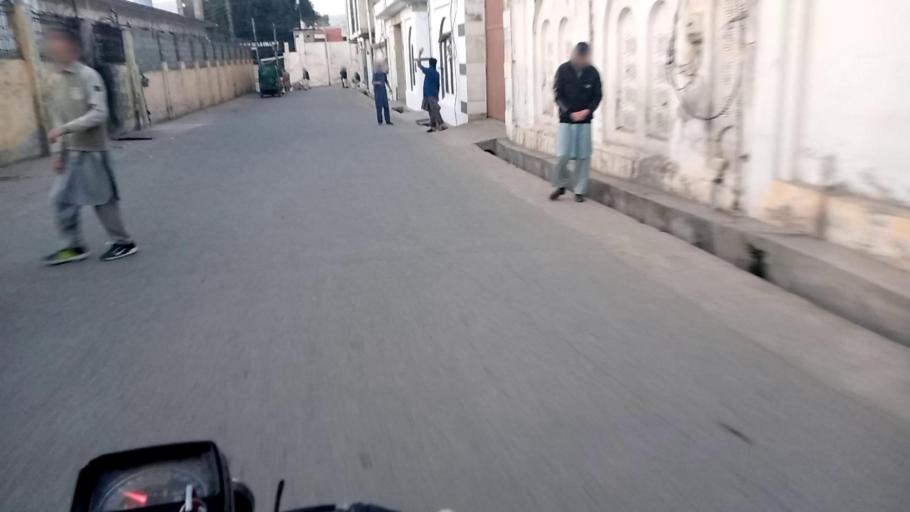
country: PK
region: Khyber Pakhtunkhwa
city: Saidu Sharif
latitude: 34.7610
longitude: 72.3608
